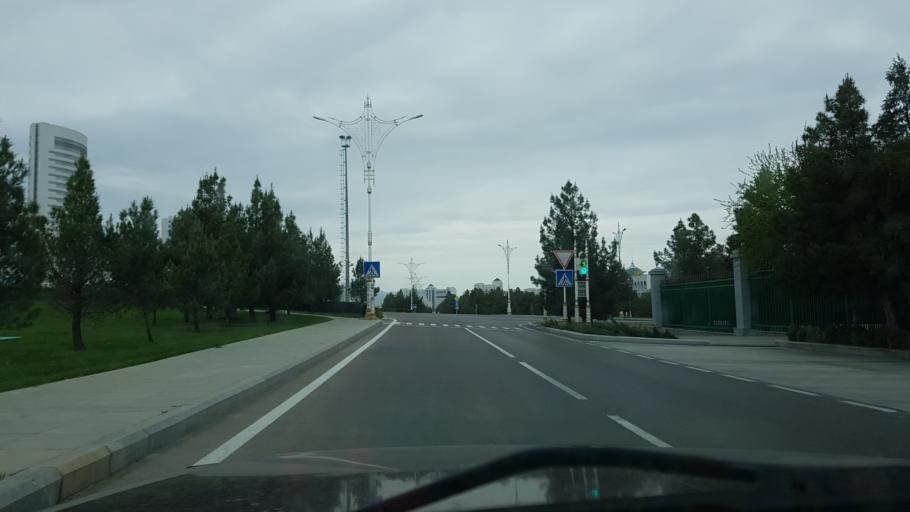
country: TM
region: Ahal
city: Ashgabat
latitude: 37.8878
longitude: 58.3532
